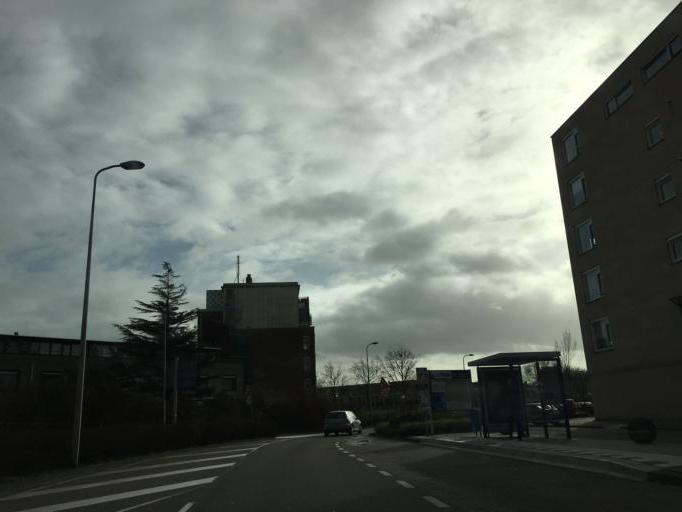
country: NL
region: South Holland
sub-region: Gemeente Capelle aan den IJssel
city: Capelle-West
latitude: 51.9184
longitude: 4.5594
